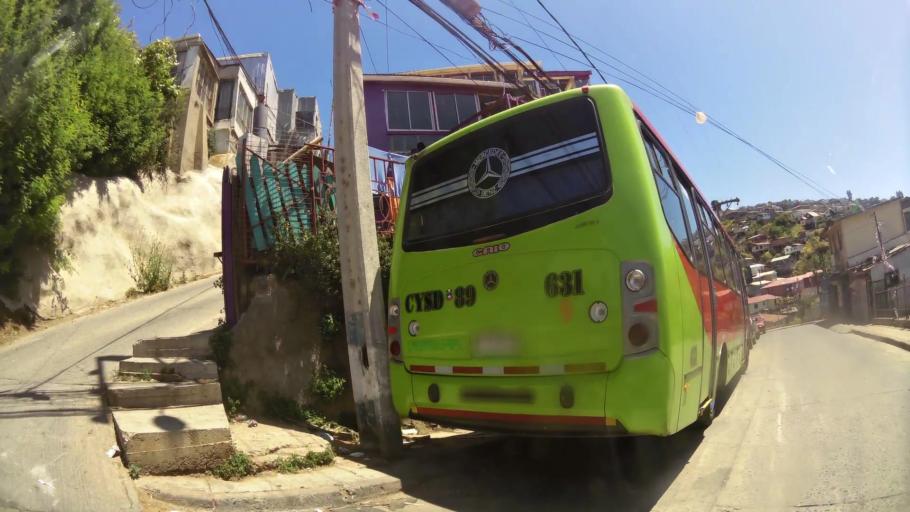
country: CL
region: Valparaiso
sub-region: Provincia de Valparaiso
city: Valparaiso
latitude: -33.0550
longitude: -71.6305
